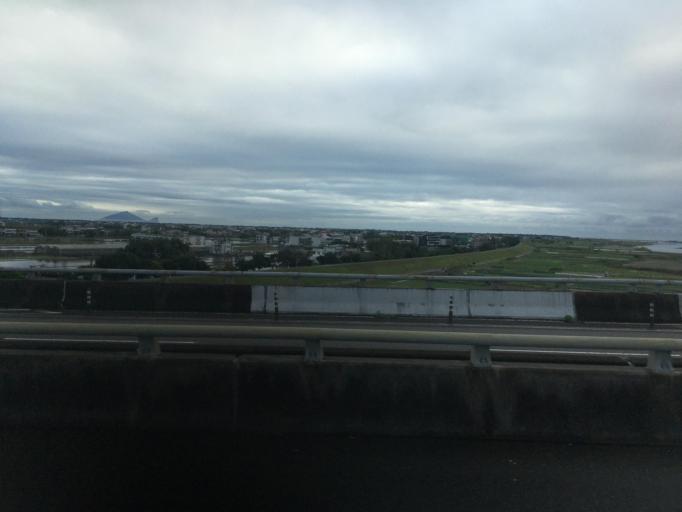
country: TW
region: Taiwan
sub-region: Yilan
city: Yilan
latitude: 24.7185
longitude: 121.7874
